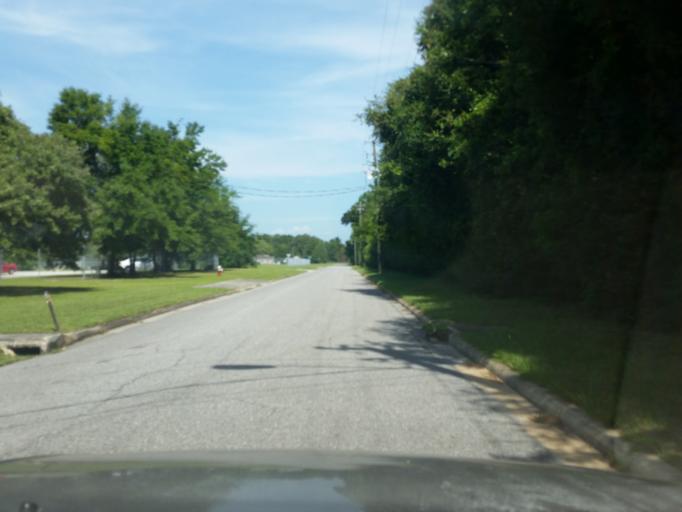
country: US
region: Florida
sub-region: Escambia County
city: Ferry Pass
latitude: 30.5318
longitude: -87.1966
